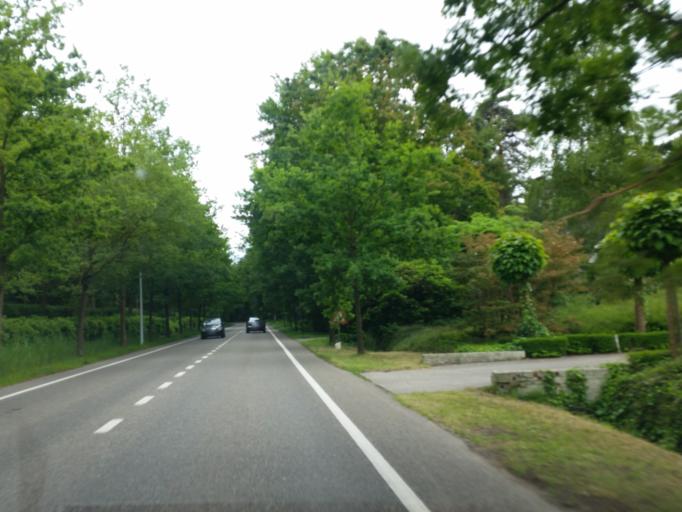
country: BE
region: Flanders
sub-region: Provincie Antwerpen
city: Schoten
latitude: 51.2722
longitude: 4.5298
